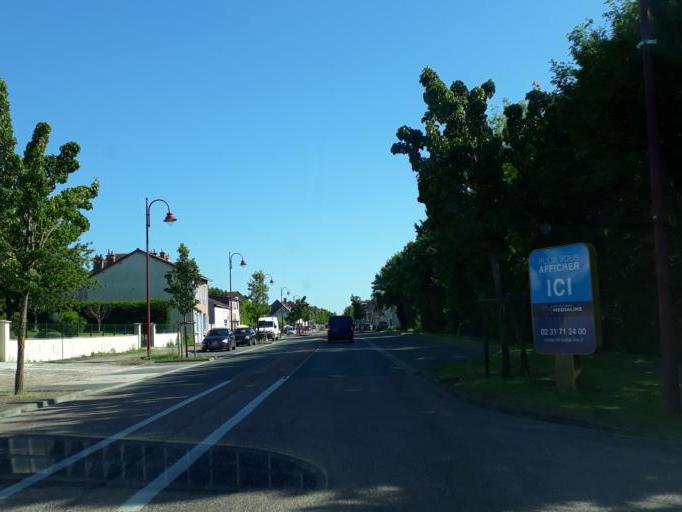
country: FR
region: Bourgogne
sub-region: Departement de la Nievre
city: Cosne-Cours-sur-Loire
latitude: 47.4505
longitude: 2.9322
